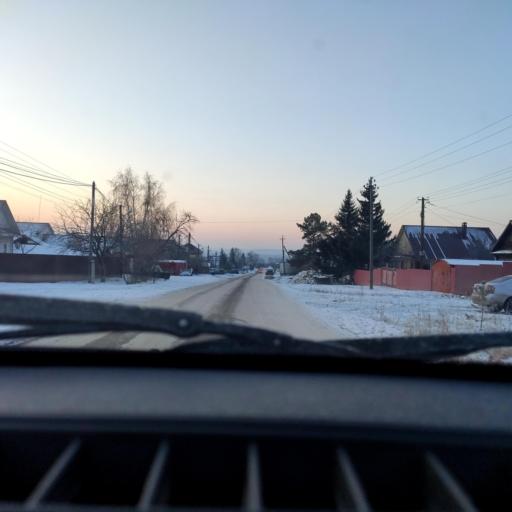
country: RU
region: Bashkortostan
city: Avdon
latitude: 54.6586
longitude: 55.7706
